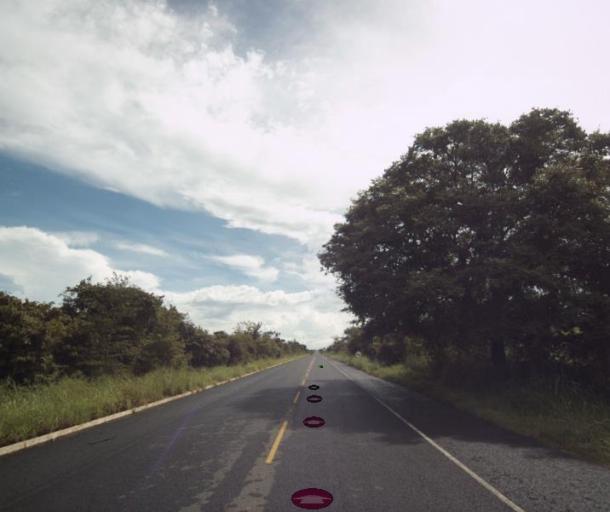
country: BR
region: Goias
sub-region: Sao Miguel Do Araguaia
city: Sao Miguel do Araguaia
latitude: -13.2956
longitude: -50.2358
